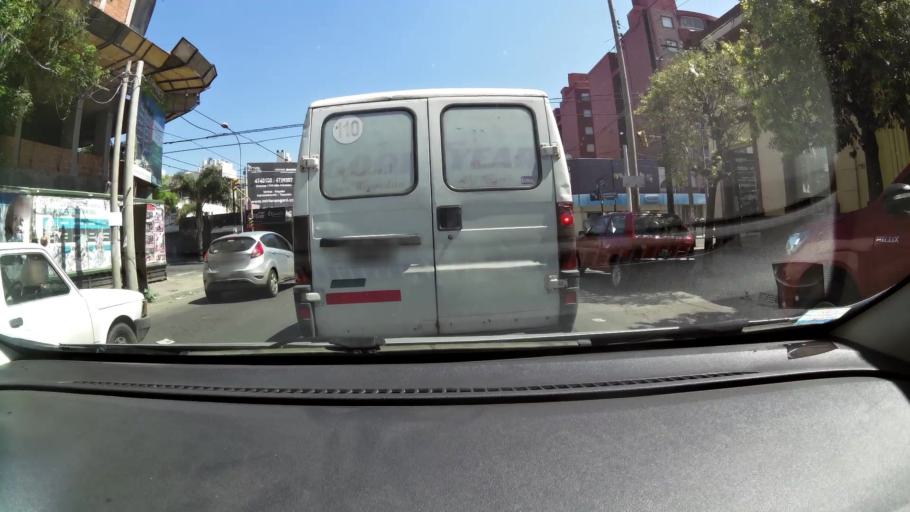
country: AR
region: Cordoba
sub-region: Departamento de Capital
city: Cordoba
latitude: -31.3966
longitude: -64.1862
